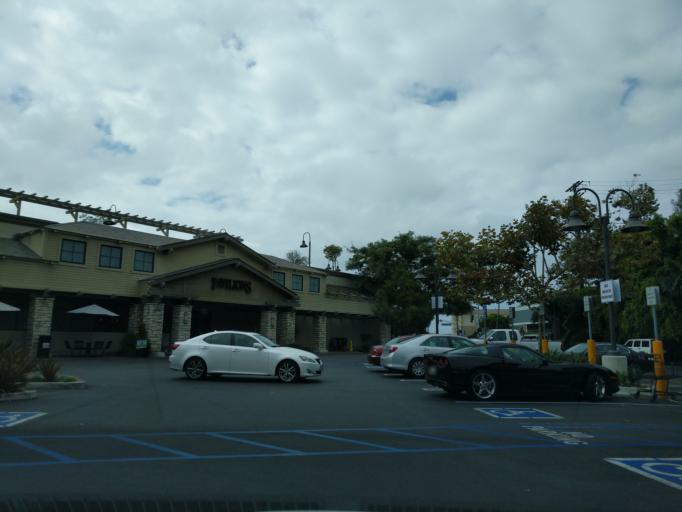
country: US
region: California
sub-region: Orange County
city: Laguna Beach
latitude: 33.5470
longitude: -117.7936
